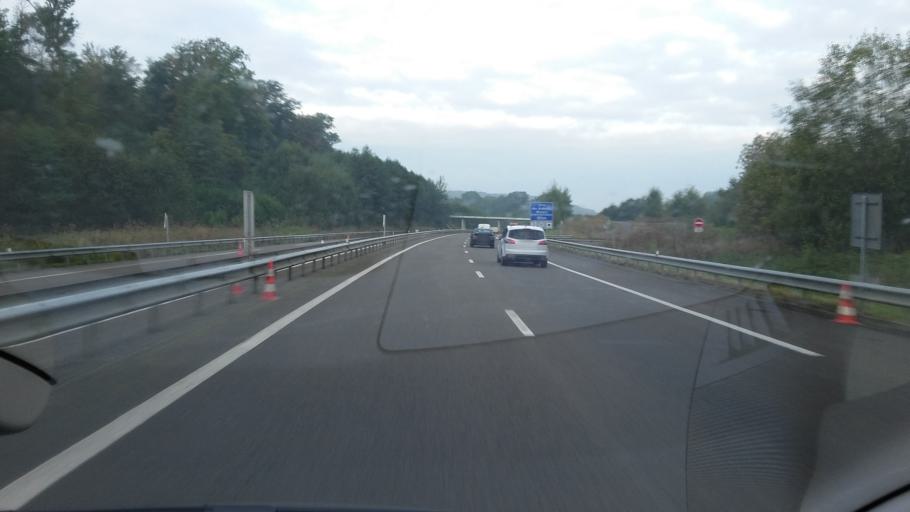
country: FR
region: Champagne-Ardenne
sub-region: Departement des Ardennes
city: La Francheville
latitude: 49.6393
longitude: 4.6142
